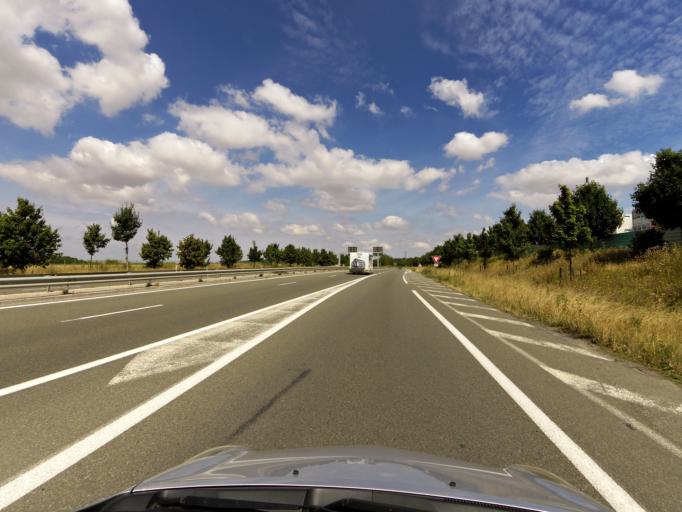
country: FR
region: Ile-de-France
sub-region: Departement de Seine-et-Marne
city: Chauconin-Neufmontiers
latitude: 48.9586
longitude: 2.8586
